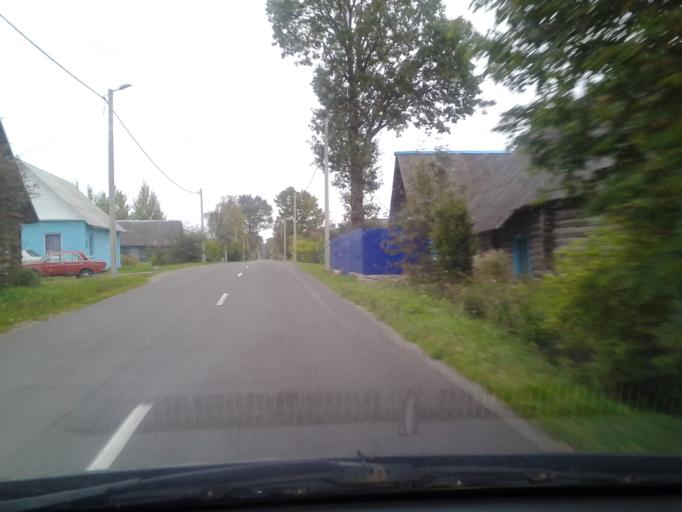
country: BY
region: Vitebsk
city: Pastavy
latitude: 55.1423
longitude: 26.9552
